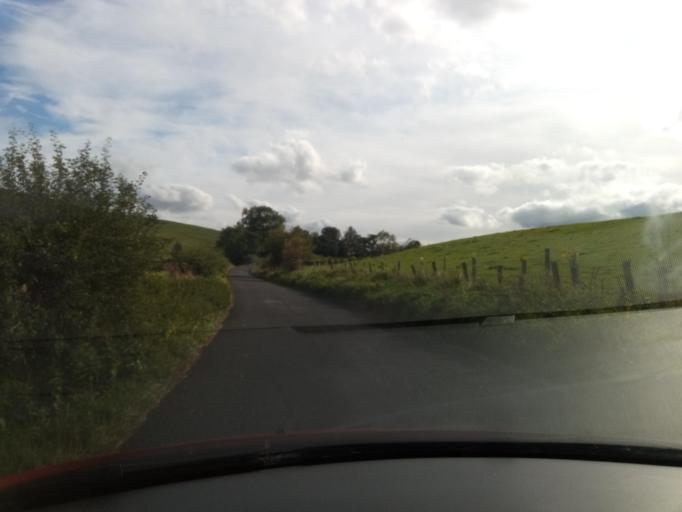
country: GB
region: Scotland
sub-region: The Scottish Borders
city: Kelso
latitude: 55.4879
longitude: -2.3483
